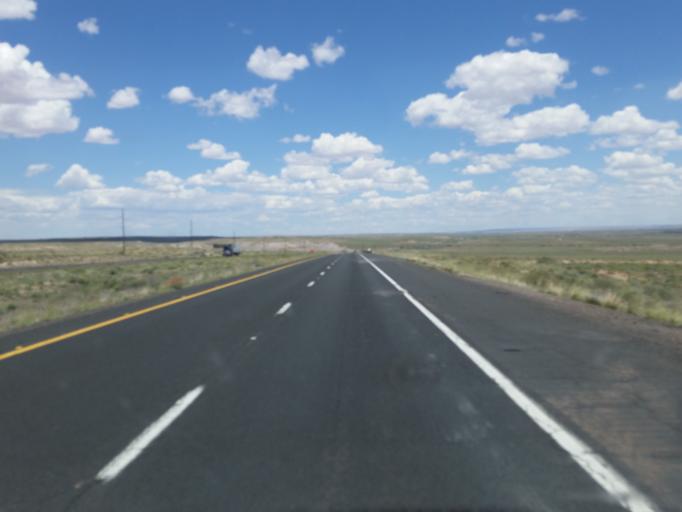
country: US
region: Arizona
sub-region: Navajo County
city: Holbrook
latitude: 34.9894
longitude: -110.0047
